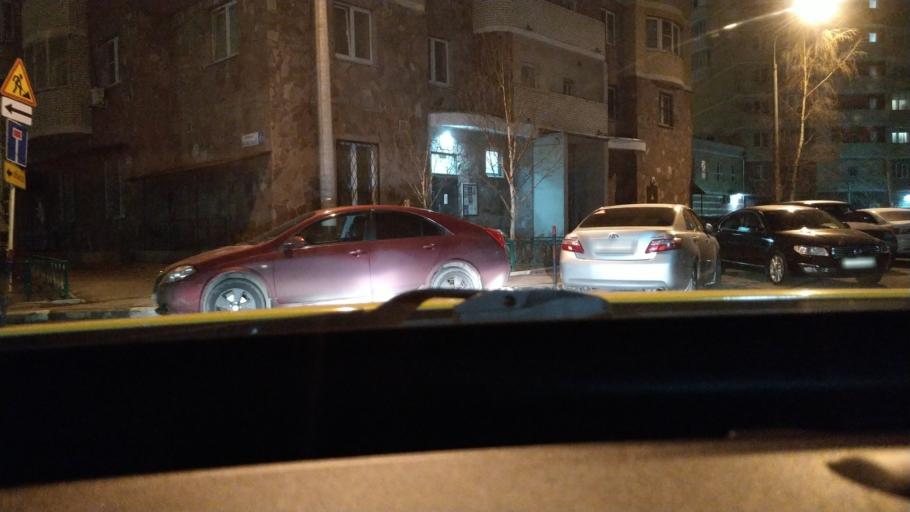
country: RU
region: Moskovskaya
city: Krasnogorsk
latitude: 55.8065
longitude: 37.3232
